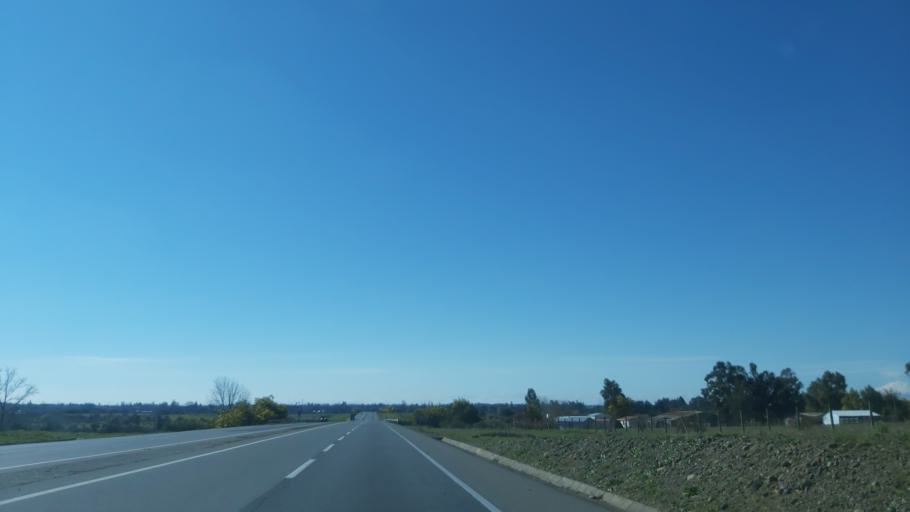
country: CL
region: Biobio
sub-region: Provincia de Nuble
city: Bulnes
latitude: -36.6588
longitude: -72.2522
